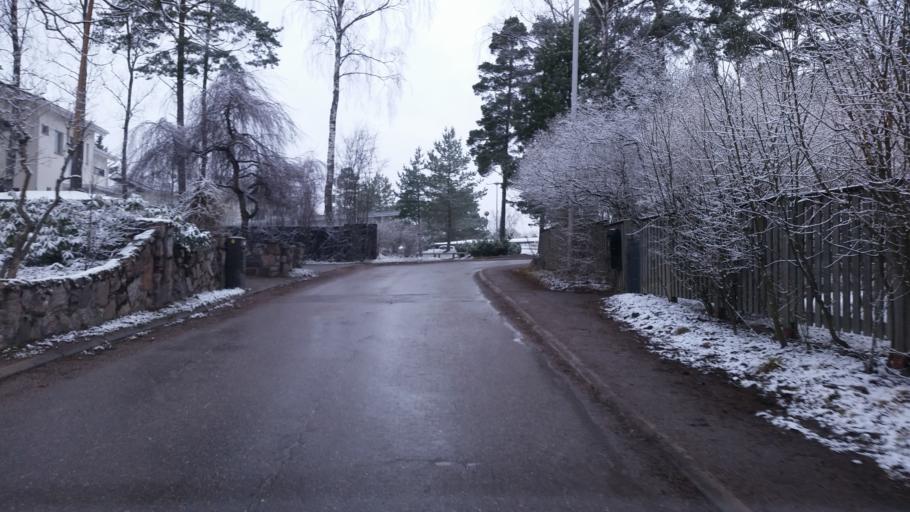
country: FI
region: Uusimaa
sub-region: Helsinki
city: Koukkuniemi
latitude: 60.1653
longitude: 24.7928
